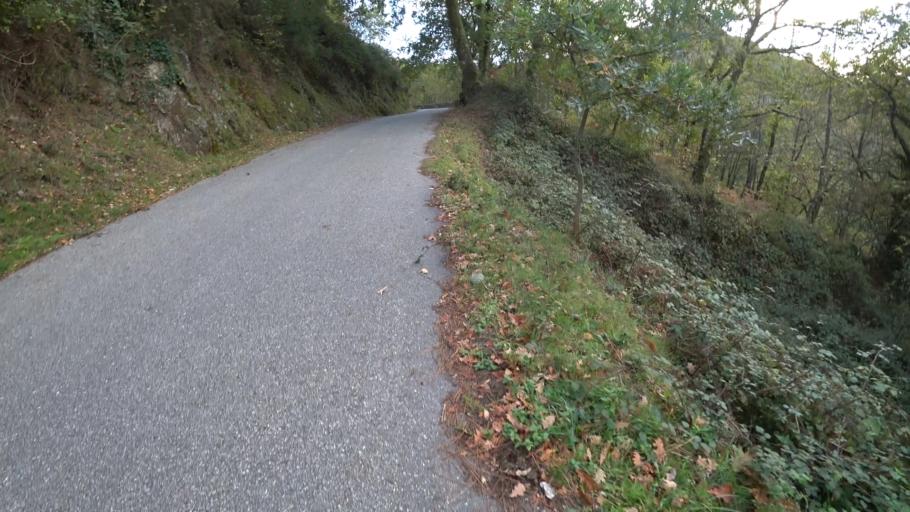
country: PT
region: Braga
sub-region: Terras de Bouro
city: Antas
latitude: 41.7626
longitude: -8.1997
